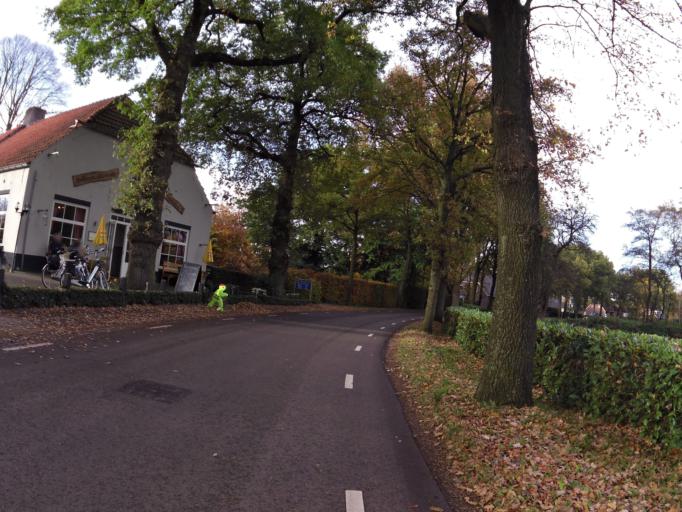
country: NL
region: North Brabant
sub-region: Gemeente Vught
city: Vught
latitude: 51.6536
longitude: 5.2354
